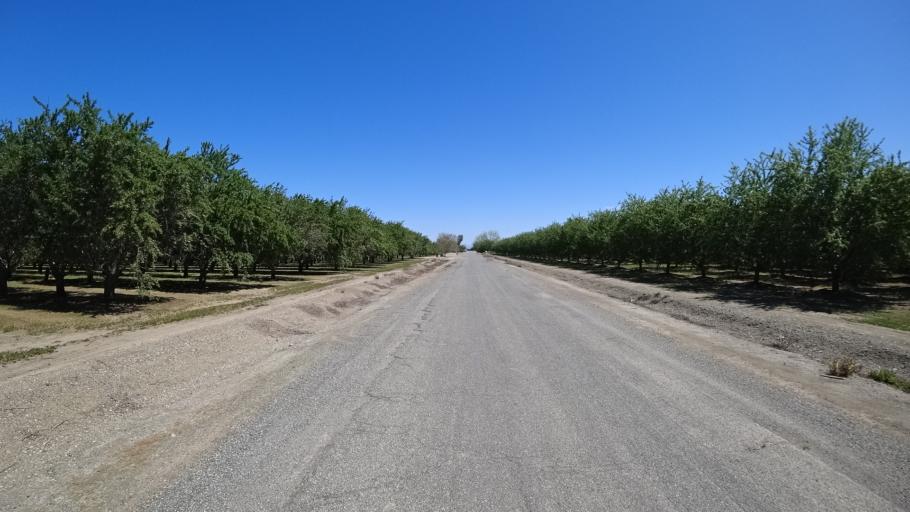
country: US
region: California
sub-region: Glenn County
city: Hamilton City
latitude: 39.7214
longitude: -122.0962
